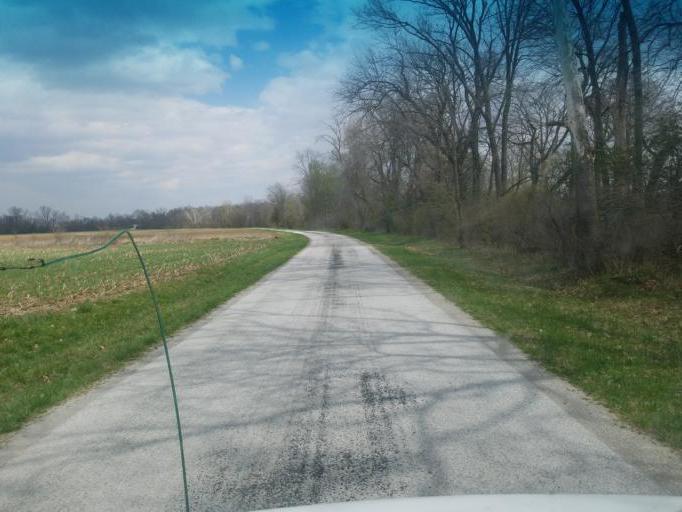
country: US
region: Ohio
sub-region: Wyandot County
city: Upper Sandusky
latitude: 40.9220
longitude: -83.2522
